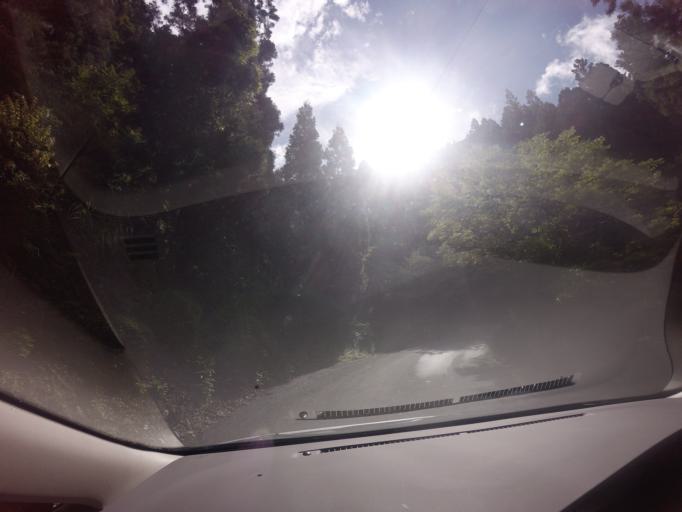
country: JP
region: Wakayama
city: Shingu
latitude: 33.9616
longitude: 135.8504
